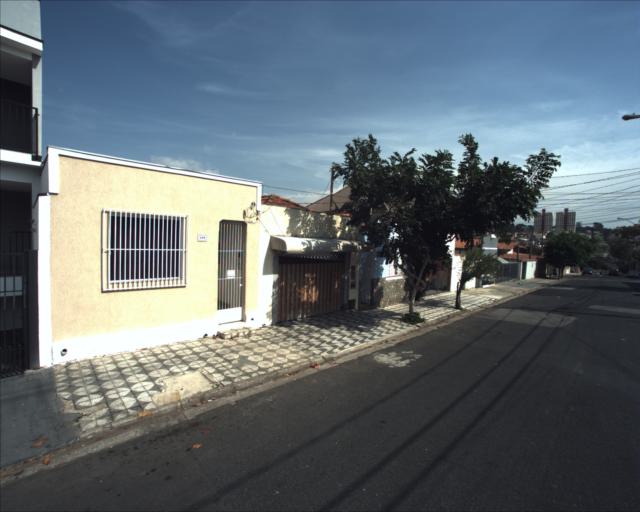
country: BR
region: Sao Paulo
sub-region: Sorocaba
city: Sorocaba
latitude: -23.4904
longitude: -47.4638
